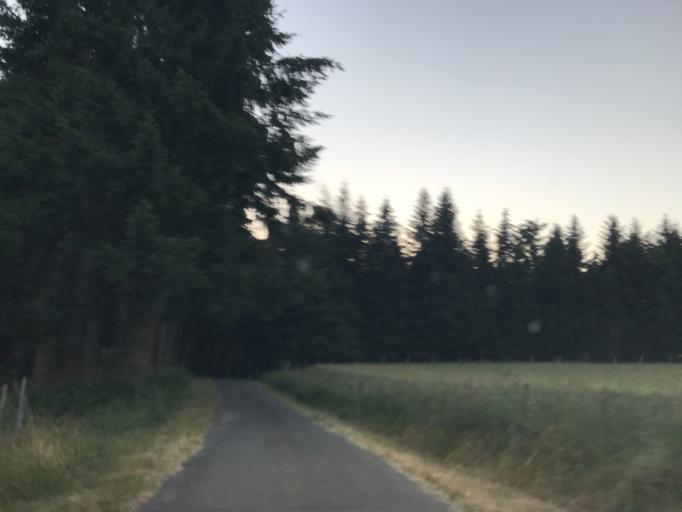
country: FR
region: Auvergne
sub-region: Departement du Puy-de-Dome
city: Celles-sur-Durolle
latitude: 45.7777
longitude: 3.6731
